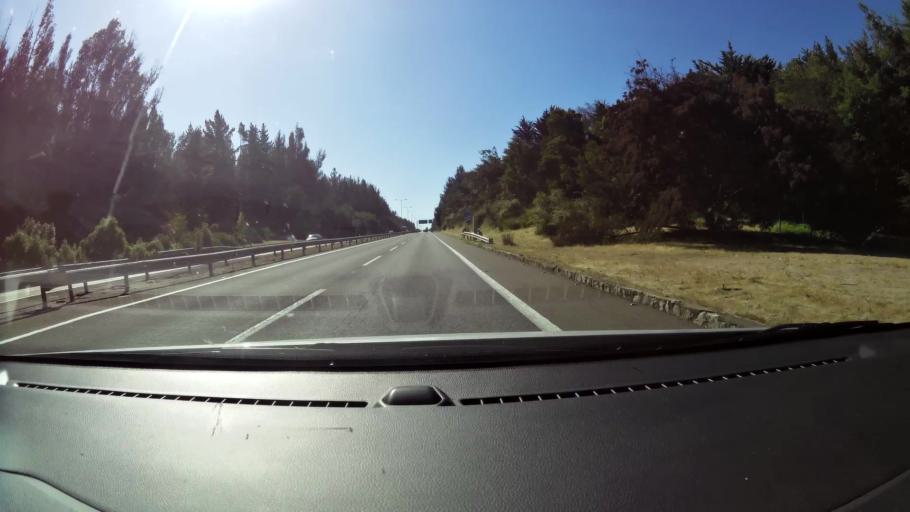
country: CL
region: Valparaiso
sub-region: Provincia de Valparaiso
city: Vina del Mar
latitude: -33.1658
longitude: -71.5329
